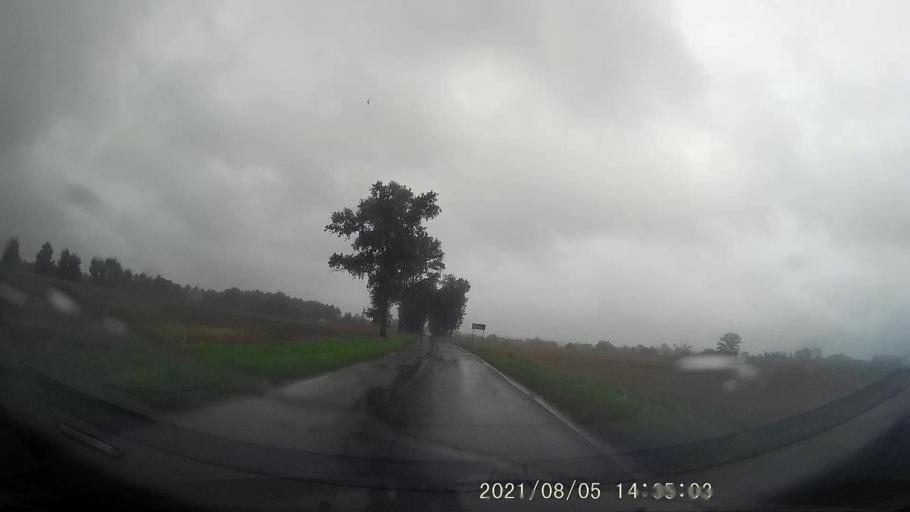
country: PL
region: Opole Voivodeship
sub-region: Powiat nyski
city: Lambinowice
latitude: 50.4674
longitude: 17.5093
